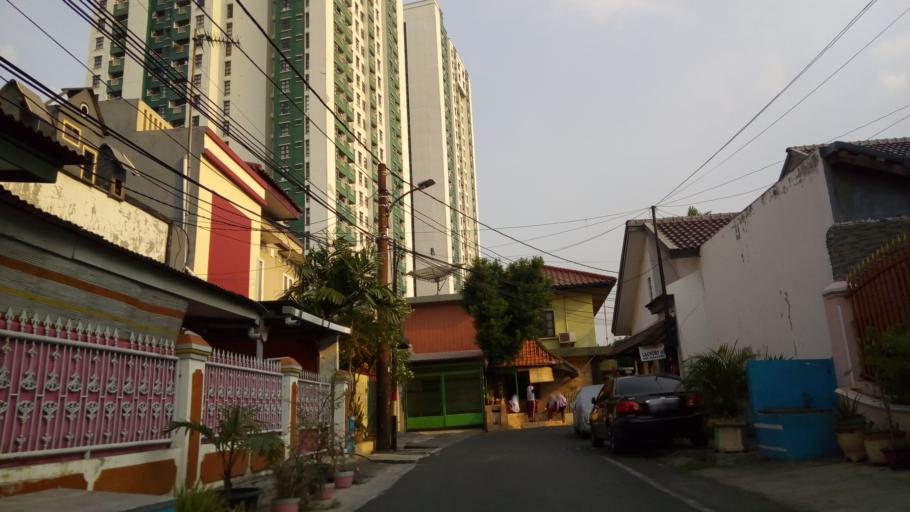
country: ID
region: Jakarta Raya
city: Jakarta
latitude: -6.1938
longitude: 106.8558
